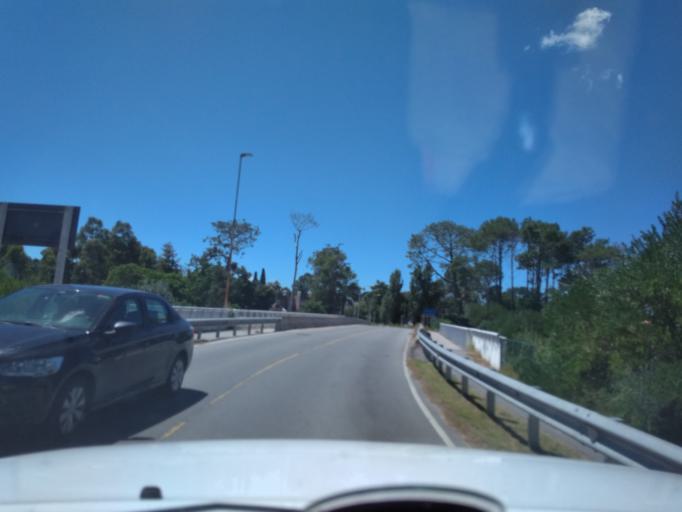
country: UY
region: Canelones
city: Barra de Carrasco
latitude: -34.8690
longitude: -56.0393
